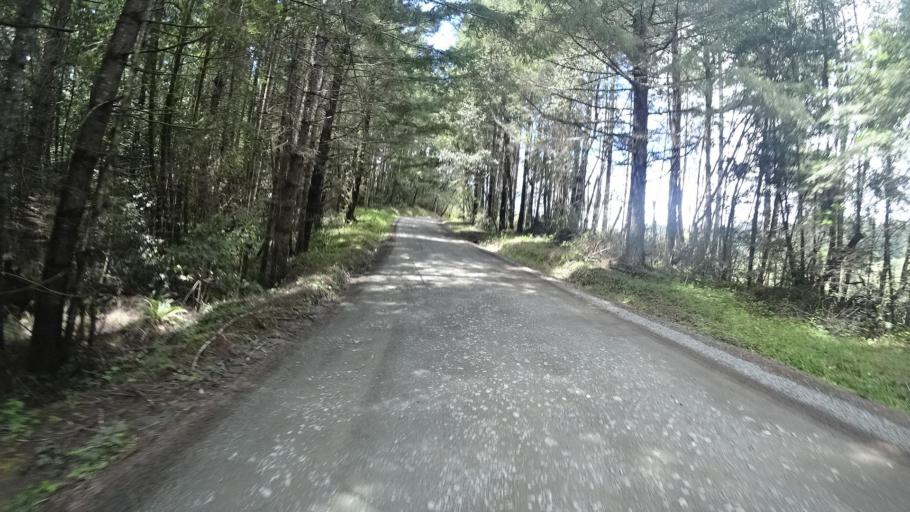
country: US
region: California
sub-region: Humboldt County
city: Blue Lake
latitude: 40.8002
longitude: -123.8759
